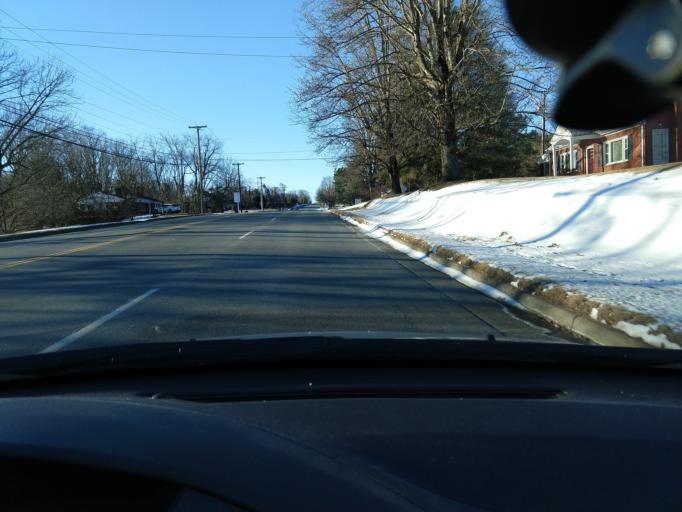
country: US
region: Virginia
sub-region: City of Bedford
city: Bedford
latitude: 37.3207
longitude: -79.5346
